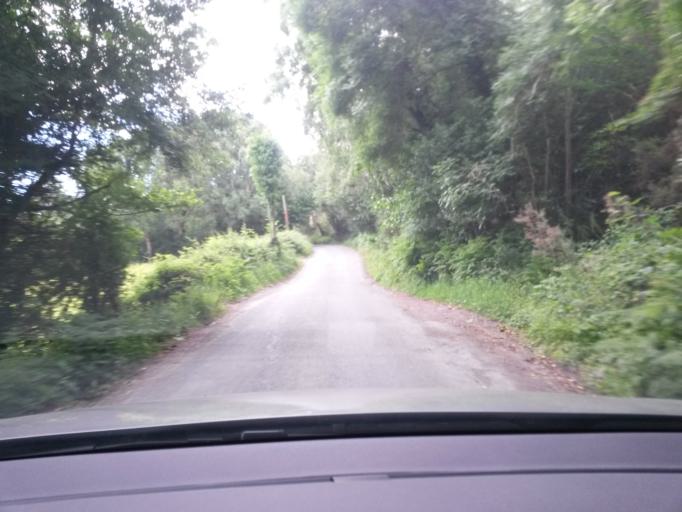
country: IE
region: Leinster
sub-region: Wicklow
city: Enniskerry
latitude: 53.1647
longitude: -6.2155
